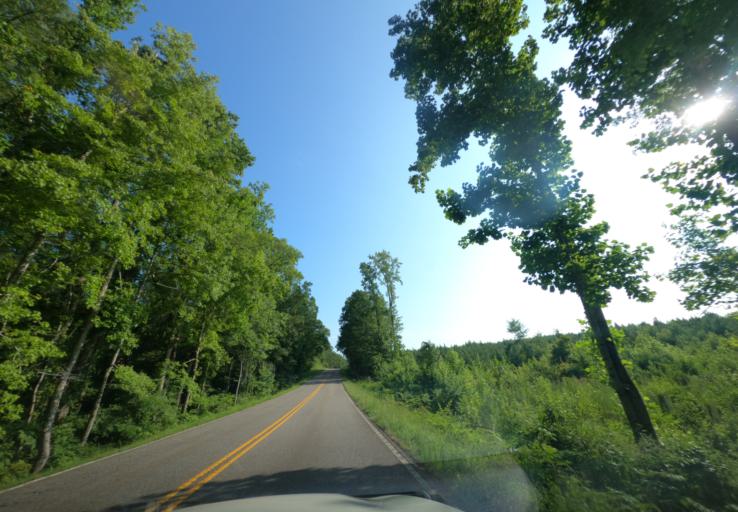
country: US
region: South Carolina
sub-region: Edgefield County
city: Edgefield
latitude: 33.7421
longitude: -81.9617
